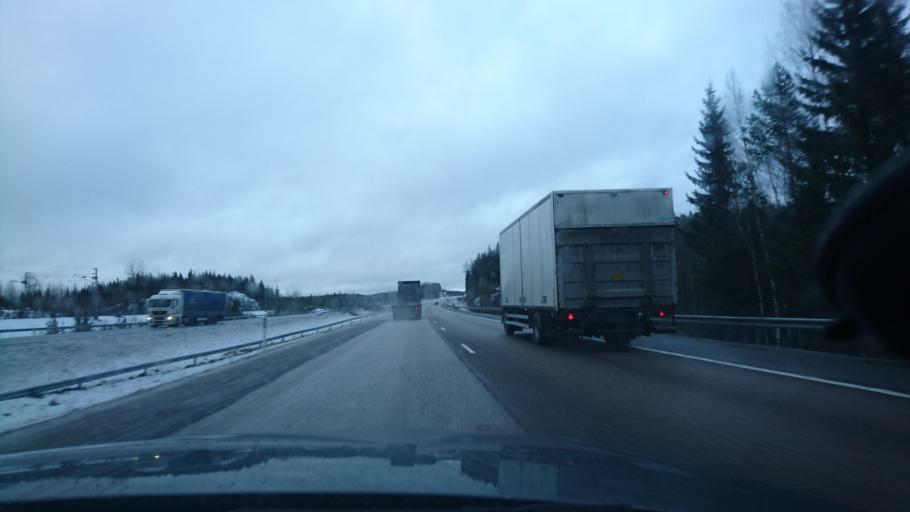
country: FI
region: Uusimaa
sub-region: Porvoo
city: Pukkila
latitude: 60.7618
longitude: 25.4634
